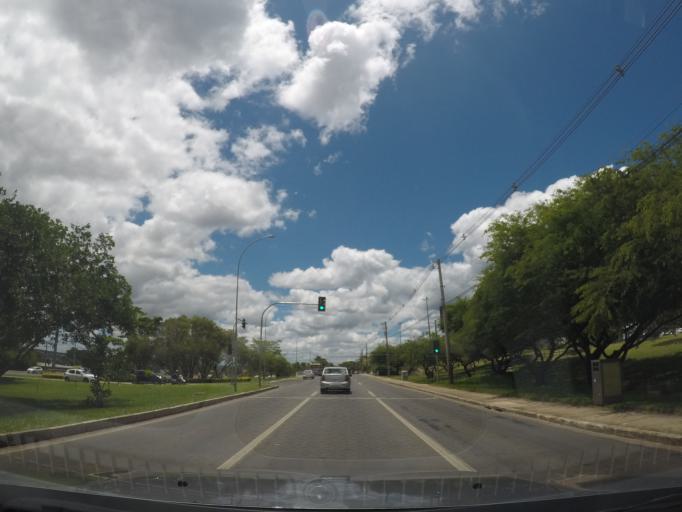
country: BR
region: Federal District
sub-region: Brasilia
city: Brasilia
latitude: -15.7221
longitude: -47.8855
